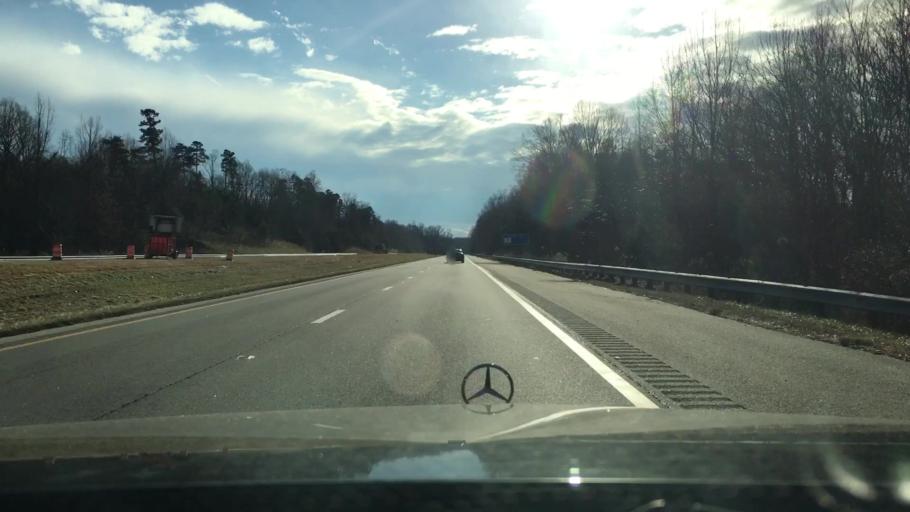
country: US
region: Virginia
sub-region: City of Danville
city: Danville
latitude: 36.5563
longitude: -79.3887
